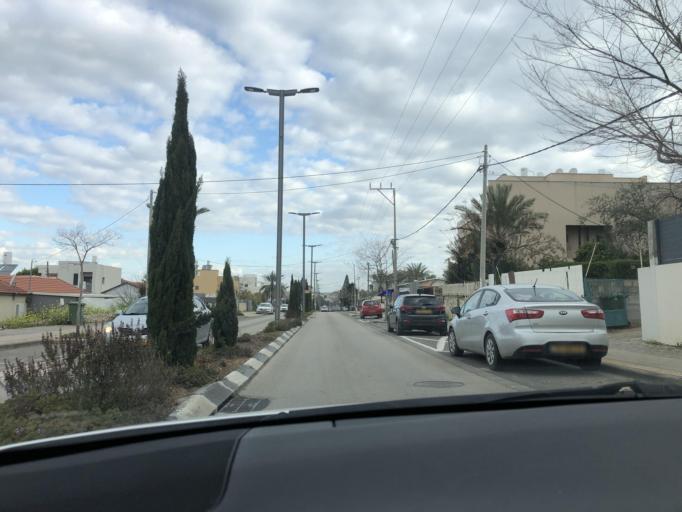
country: IL
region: Central District
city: Rosh Ha'Ayin
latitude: 32.0962
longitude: 34.9545
